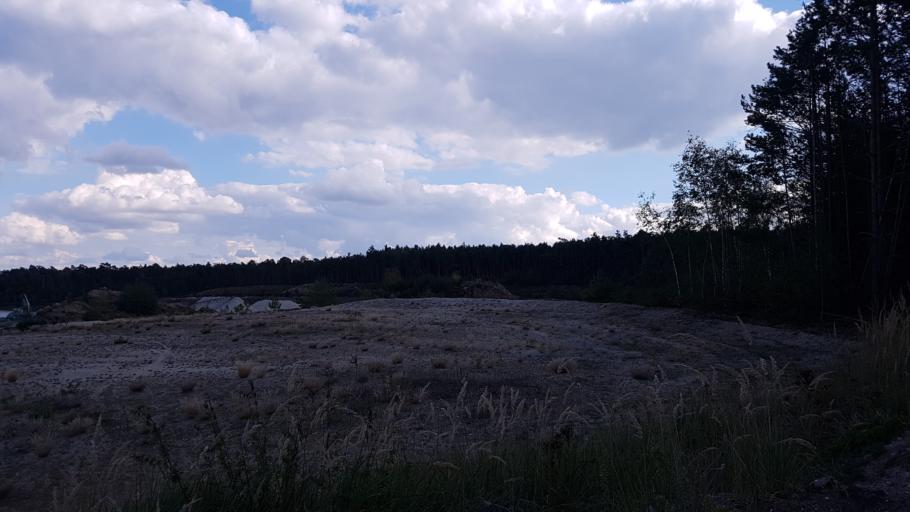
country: DE
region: Brandenburg
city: Sonnewalde
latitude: 51.6375
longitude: 13.6488
